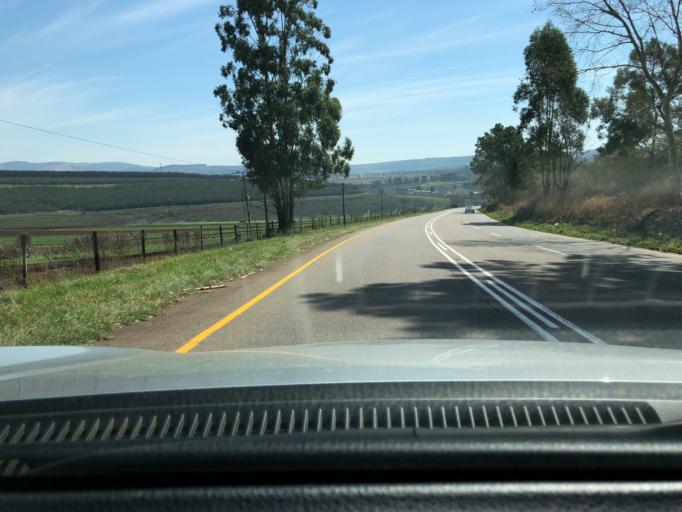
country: ZA
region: KwaZulu-Natal
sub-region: uMgungundlovu District Municipality
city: Richmond
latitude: -29.7826
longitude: 30.3523
